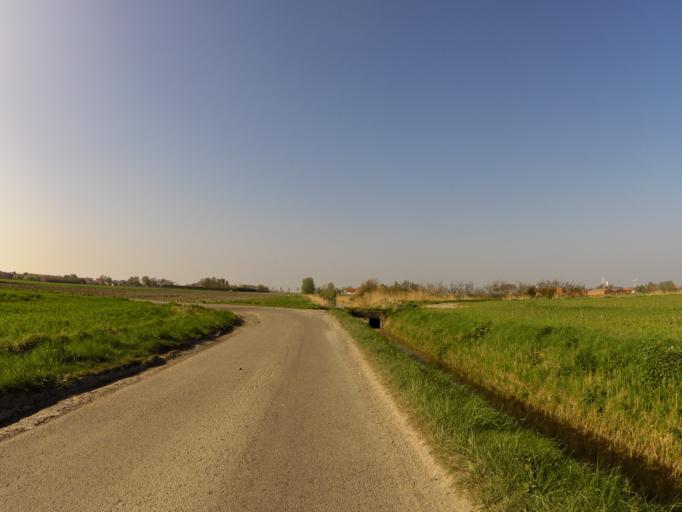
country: BE
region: Flanders
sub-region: Provincie West-Vlaanderen
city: Gistel
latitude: 51.1345
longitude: 2.9318
